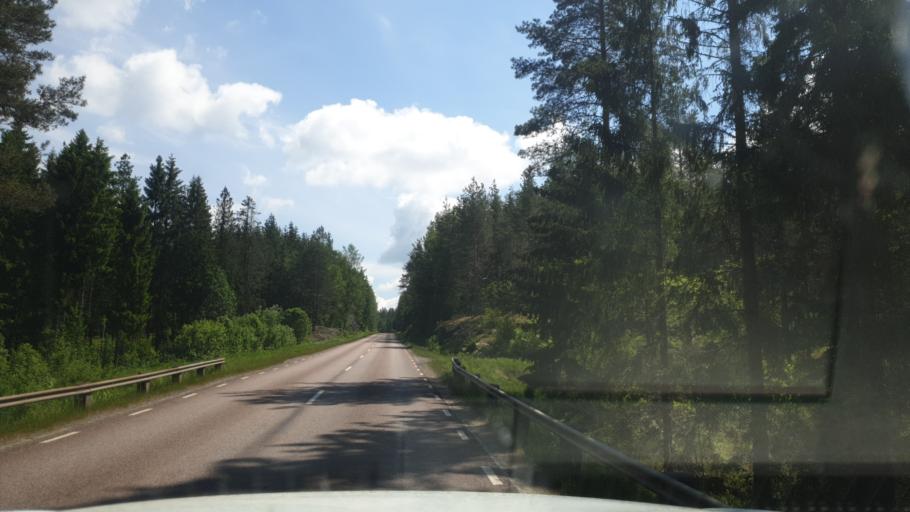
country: SE
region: Vaermland
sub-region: Grums Kommun
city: Slottsbron
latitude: 59.4036
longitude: 13.0113
